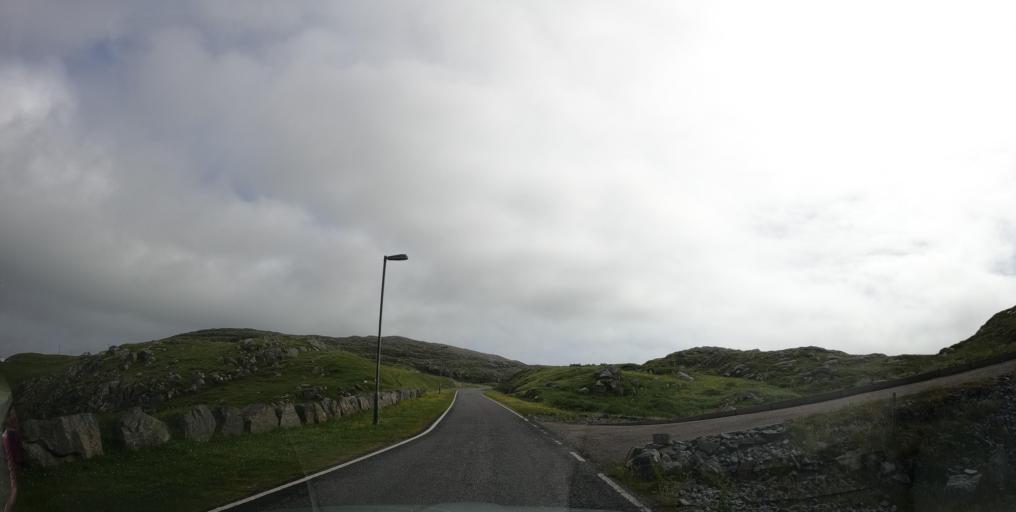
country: GB
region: Scotland
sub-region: Eilean Siar
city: Isle of South Uist
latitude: 57.0723
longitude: -7.3047
